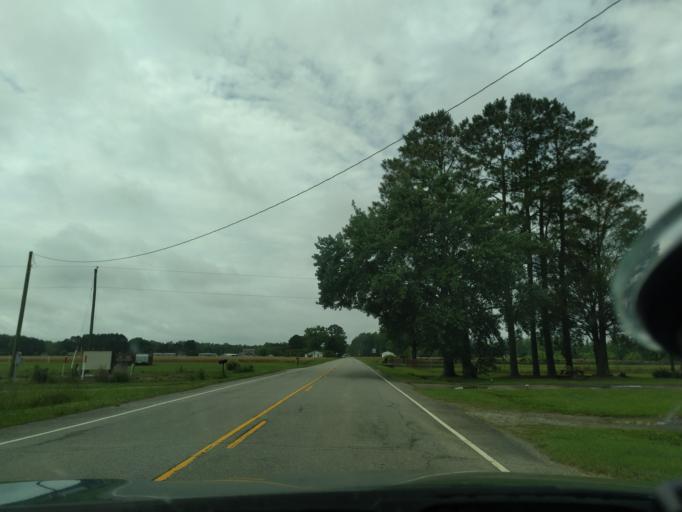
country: US
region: North Carolina
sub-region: Chowan County
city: Edenton
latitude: 35.9168
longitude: -76.6002
